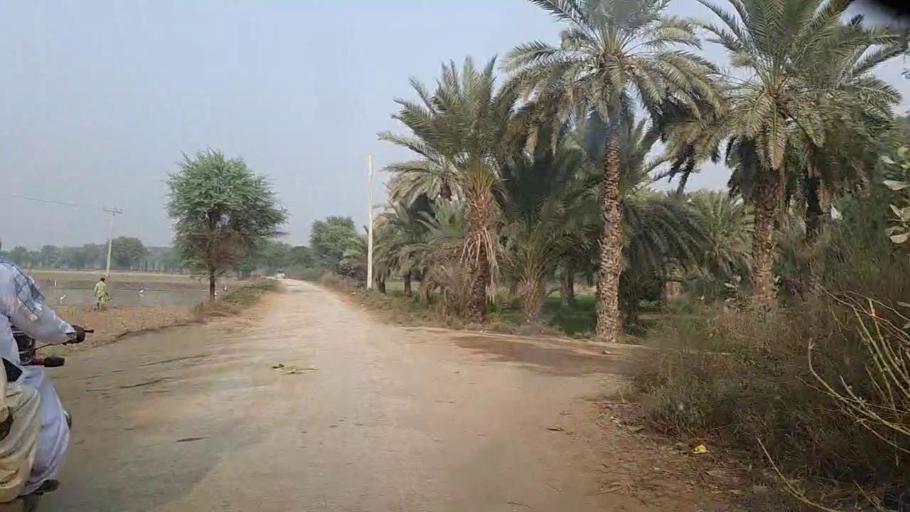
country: PK
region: Sindh
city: Bozdar
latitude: 27.1449
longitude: 68.6686
